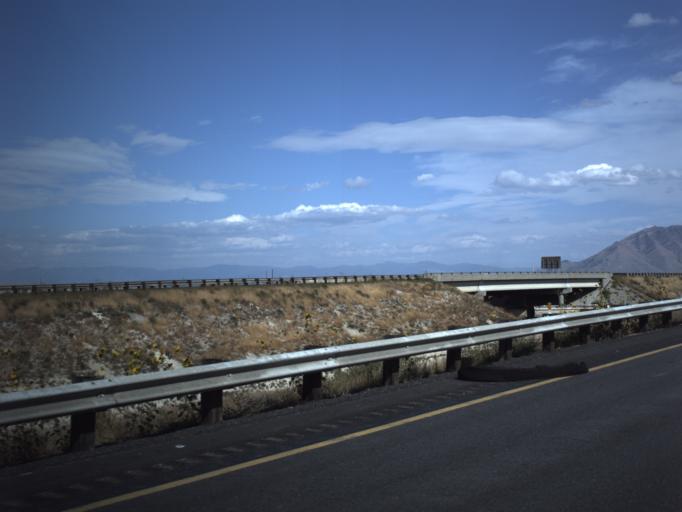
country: US
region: Utah
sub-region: Tooele County
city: Grantsville
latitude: 40.6842
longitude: -112.4424
